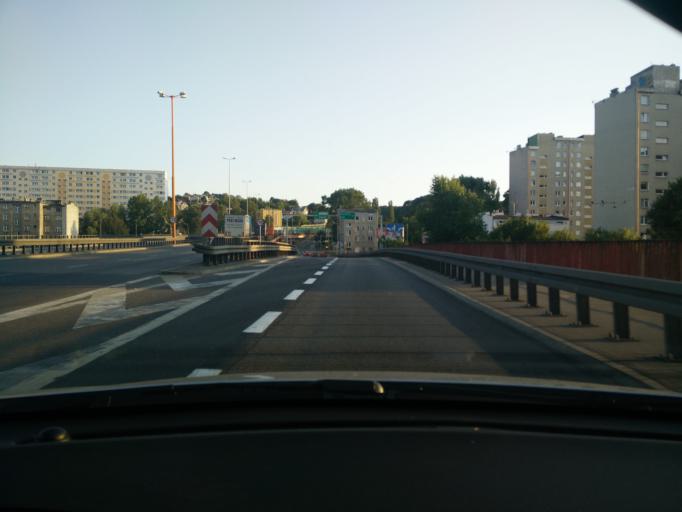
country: PL
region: Pomeranian Voivodeship
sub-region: Gdynia
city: Pogorze
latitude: 54.5346
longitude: 18.4902
